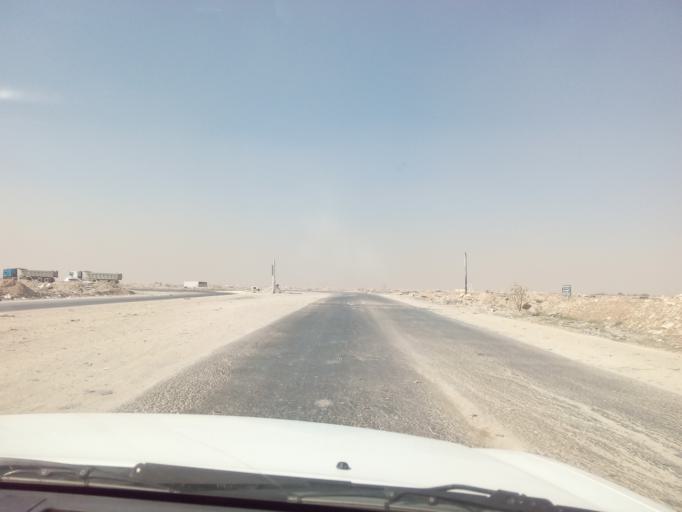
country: SA
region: Ar Riyad
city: Riyadh
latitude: 24.6387
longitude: 46.8838
